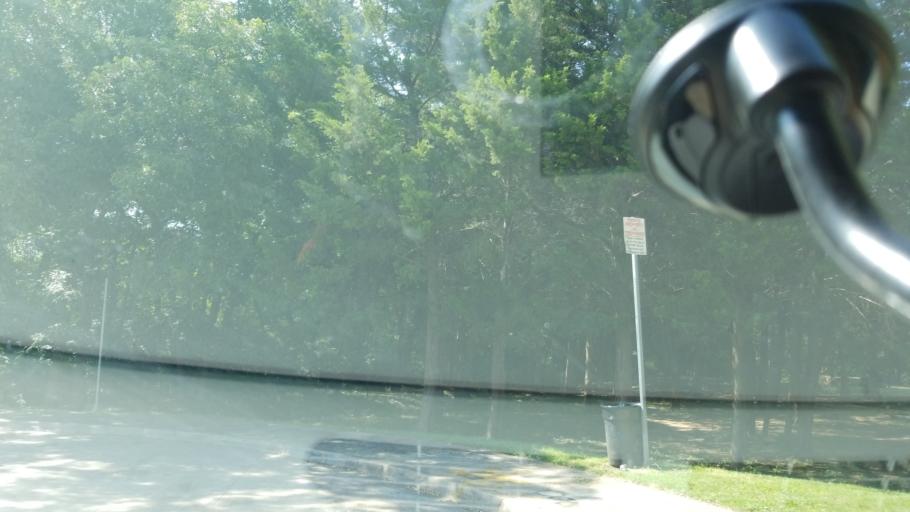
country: US
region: Texas
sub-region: Dallas County
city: Cockrell Hill
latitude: 32.7105
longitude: -96.8703
